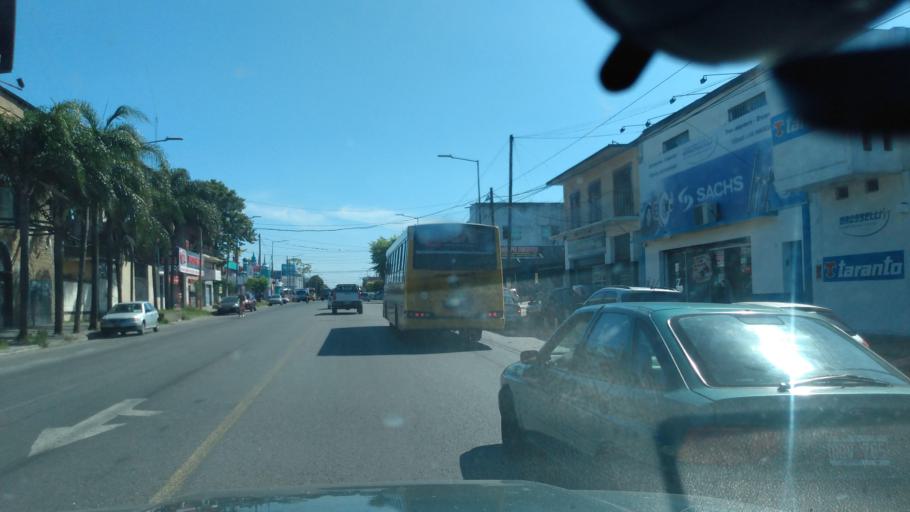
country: AR
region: Buenos Aires
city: Hurlingham
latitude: -34.5482
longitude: -58.7185
